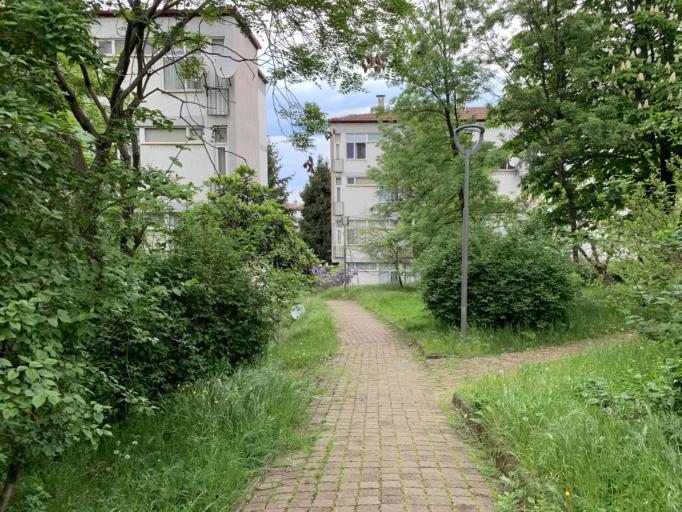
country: TR
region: Trabzon
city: Trabzon
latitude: 40.9950
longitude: 39.7664
